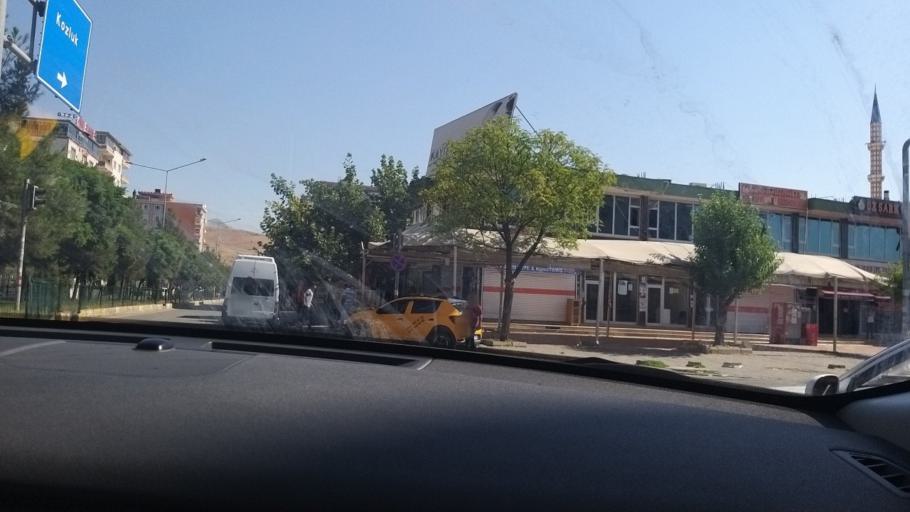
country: TR
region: Batman
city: Kozluk
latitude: 38.1663
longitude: 41.5011
